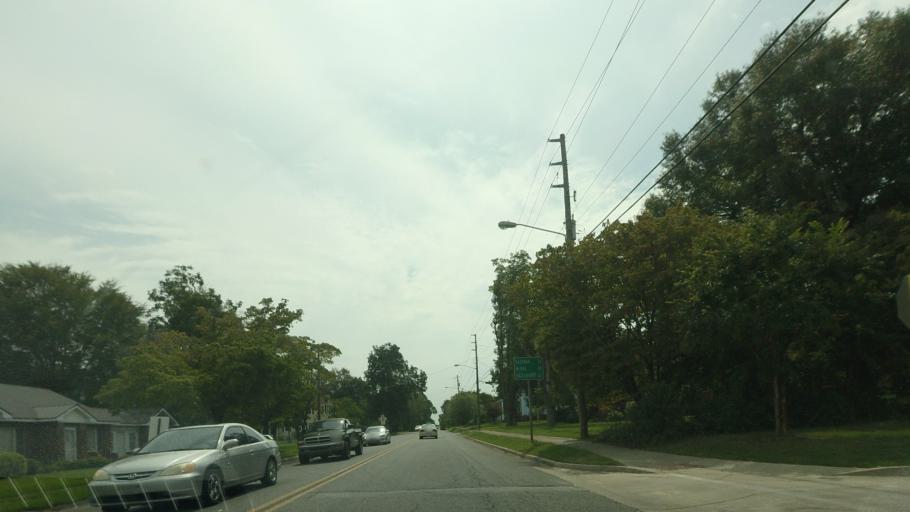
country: US
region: Georgia
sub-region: Bleckley County
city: Cochran
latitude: 32.3862
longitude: -83.3543
